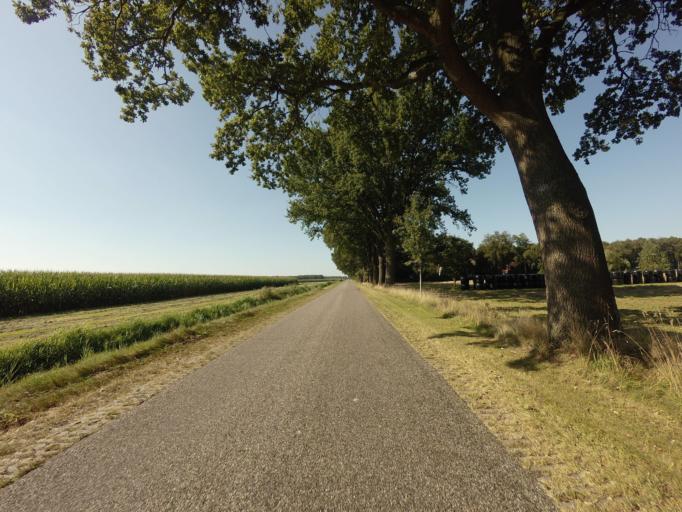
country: DE
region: Lower Saxony
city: Wielen
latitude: 52.5214
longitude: 6.6617
